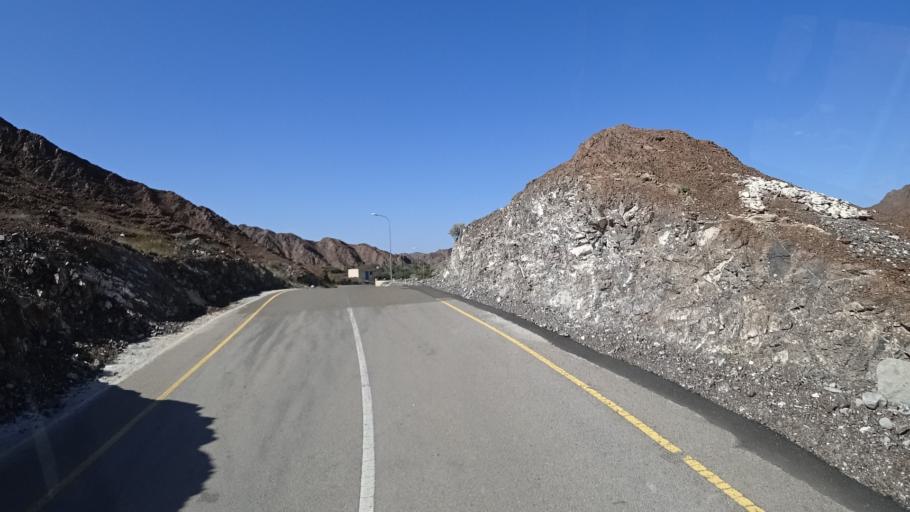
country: OM
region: Al Batinah
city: Bayt al `Awabi
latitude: 23.3757
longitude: 57.6651
